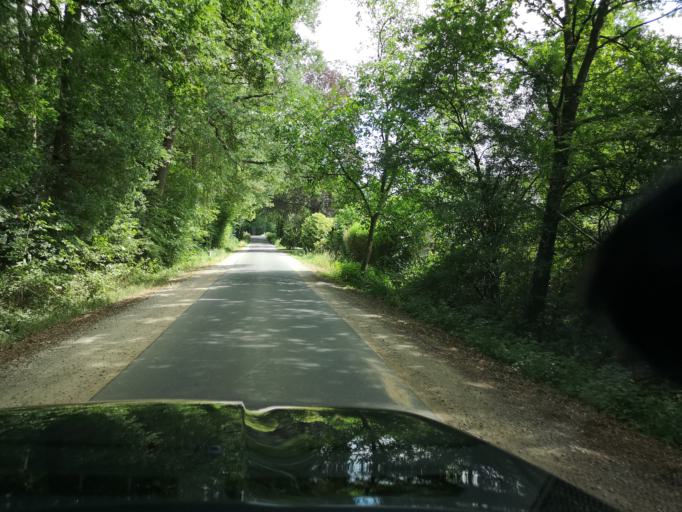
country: DE
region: North Rhine-Westphalia
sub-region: Regierungsbezirk Dusseldorf
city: Wesel
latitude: 51.7026
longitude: 6.6289
